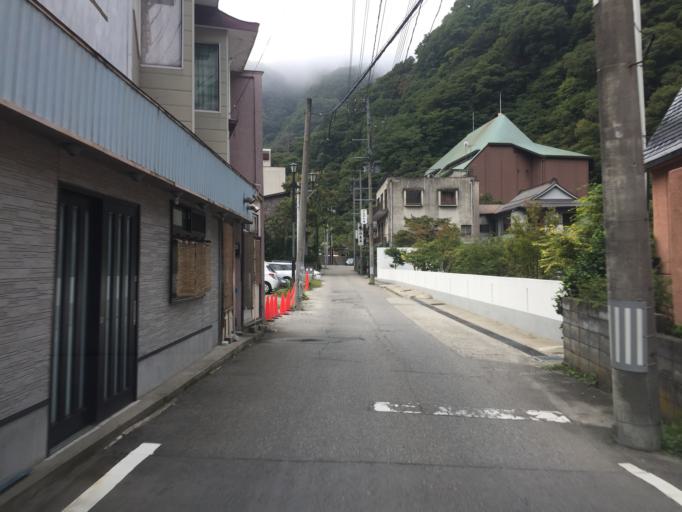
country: JP
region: Fukushima
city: Inawashiro
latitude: 37.4749
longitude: 139.9625
